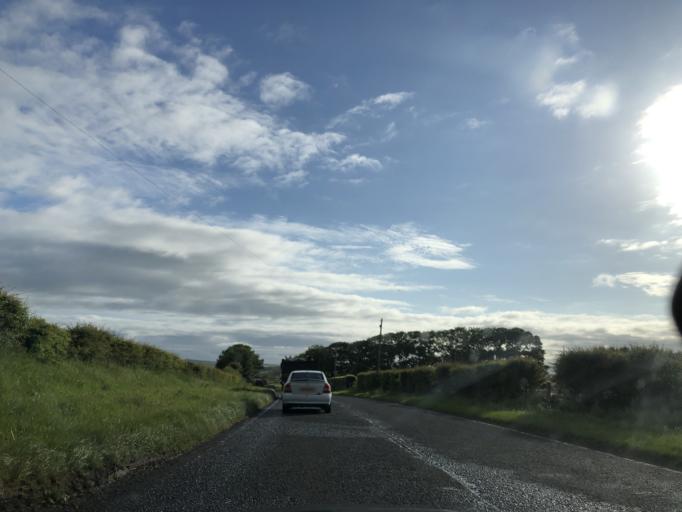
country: GB
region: Northern Ireland
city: Bushmills
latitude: 55.1880
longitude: -6.5499
